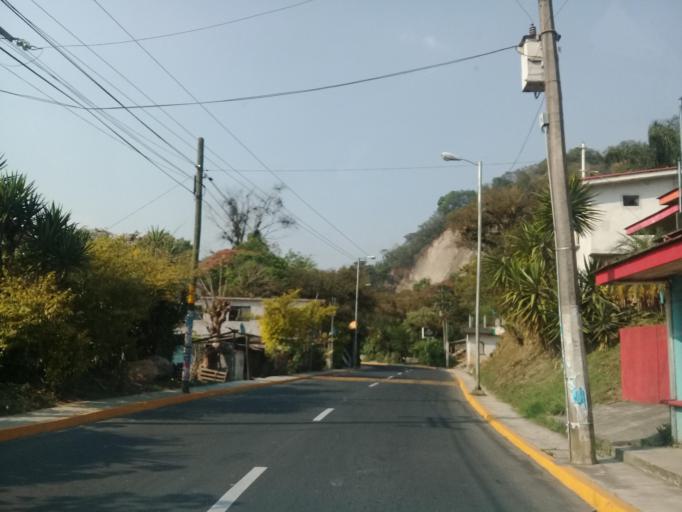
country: MX
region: Veracruz
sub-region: Ixtaczoquitlan
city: Campo Chico
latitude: 18.8490
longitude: -97.0368
